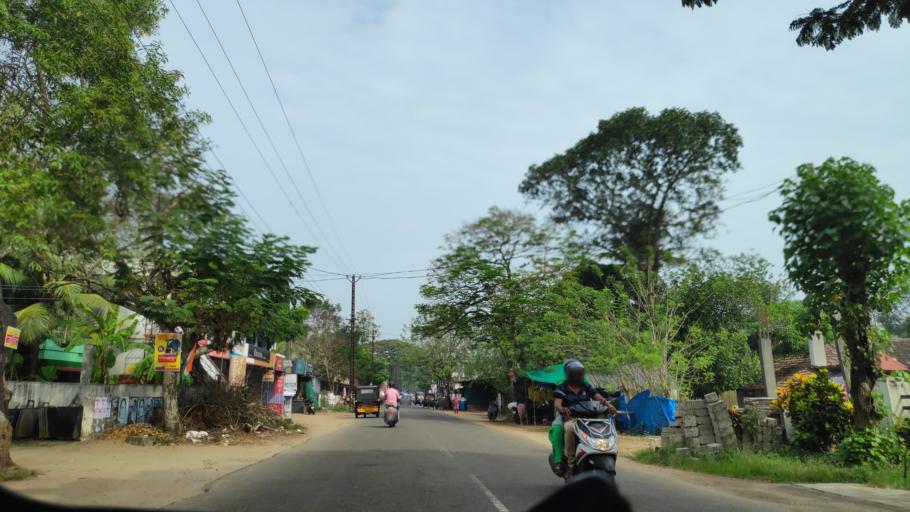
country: IN
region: Kerala
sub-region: Alappuzha
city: Kutiatodu
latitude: 9.7988
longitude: 76.3539
